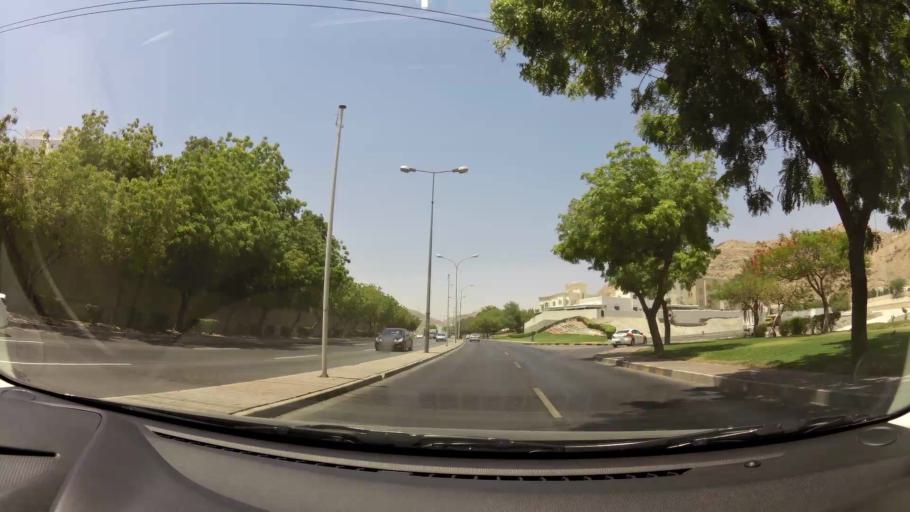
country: OM
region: Muhafazat Masqat
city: Muscat
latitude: 23.6077
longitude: 58.5377
